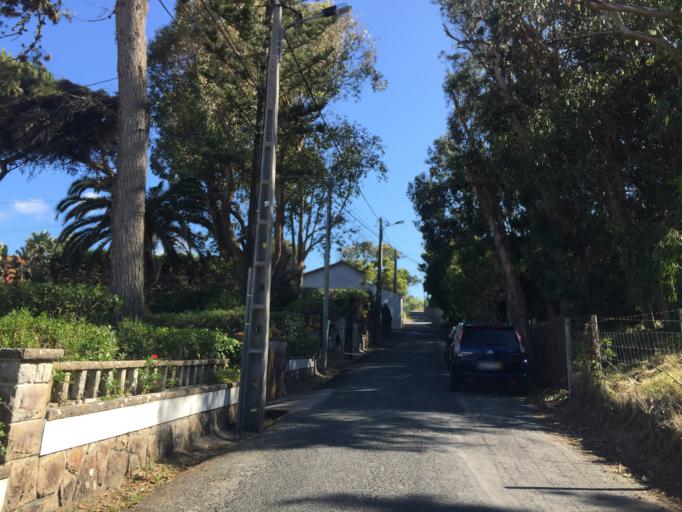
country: PT
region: Lisbon
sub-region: Sintra
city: Colares
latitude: 38.8166
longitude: -9.4699
